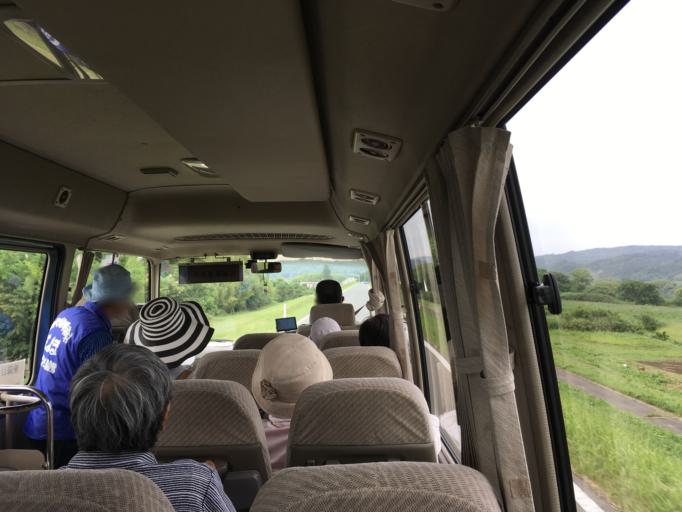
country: JP
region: Miyagi
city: Wakuya
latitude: 38.7298
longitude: 141.2643
